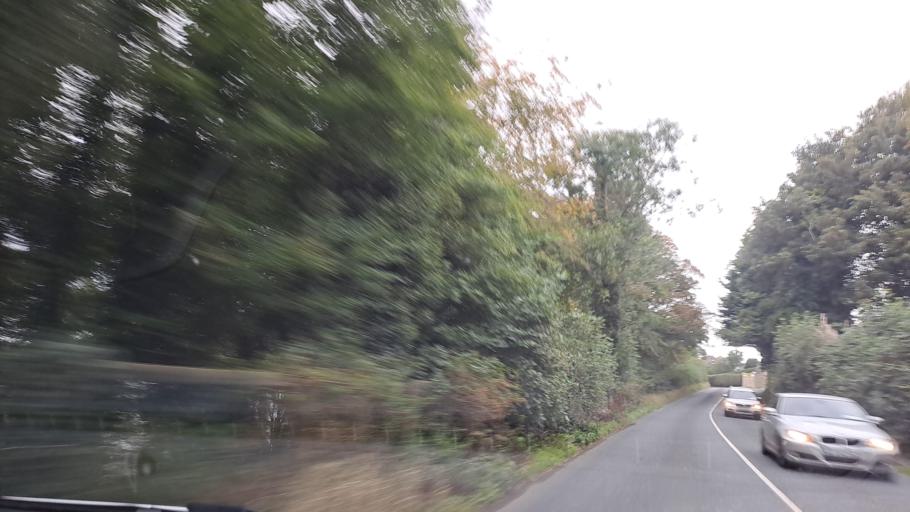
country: IE
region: Ulster
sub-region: An Cabhan
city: Bailieborough
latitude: 54.0000
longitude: -6.9028
